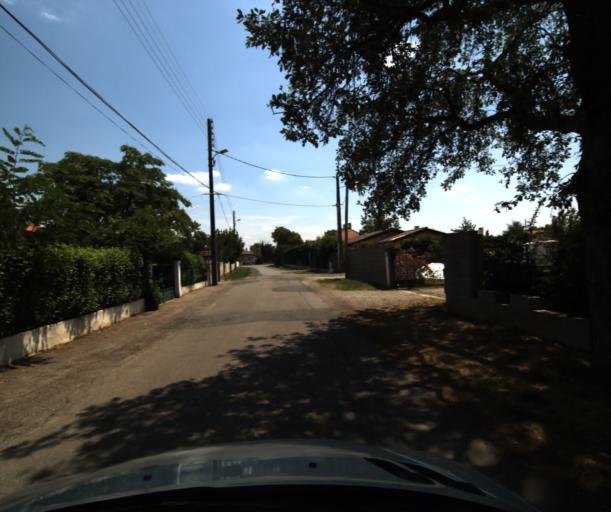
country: FR
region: Midi-Pyrenees
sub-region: Departement de la Haute-Garonne
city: Saint-Lys
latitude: 43.5105
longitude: 1.1781
